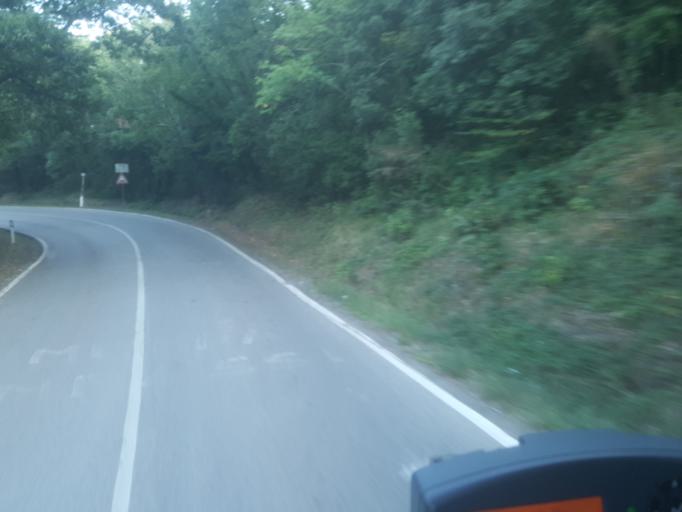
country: IT
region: Tuscany
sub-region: Province of Florence
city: Montaione
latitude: 43.5313
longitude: 10.9243
